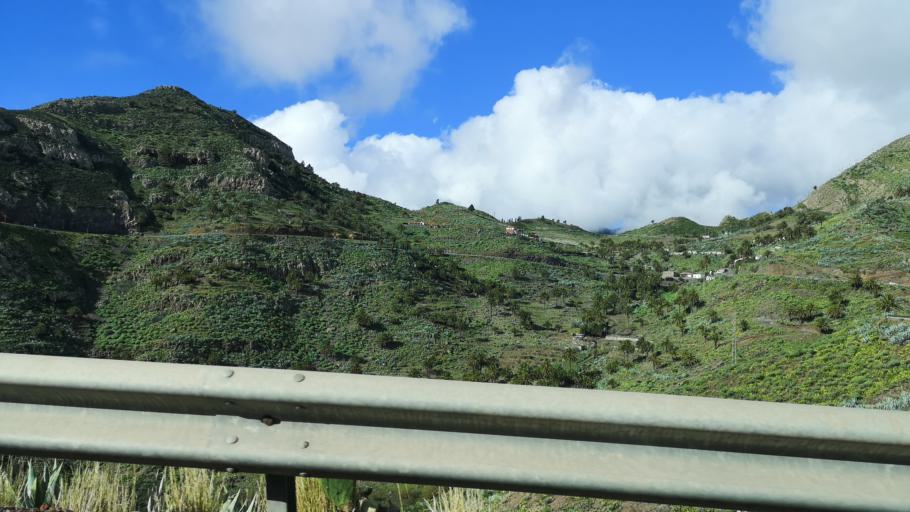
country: ES
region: Canary Islands
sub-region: Provincia de Santa Cruz de Tenerife
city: Alajero
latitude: 28.0937
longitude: -17.1971
